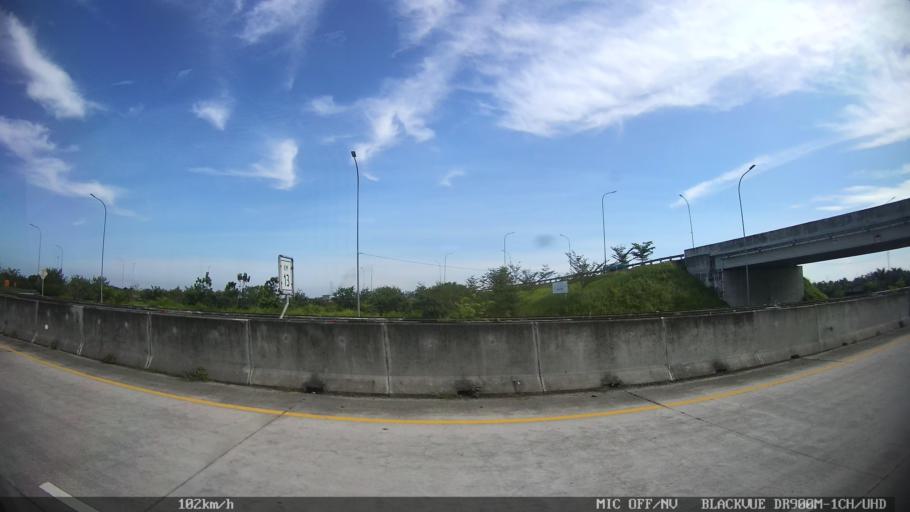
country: ID
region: North Sumatra
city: Sunggal
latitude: 3.6372
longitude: 98.5845
